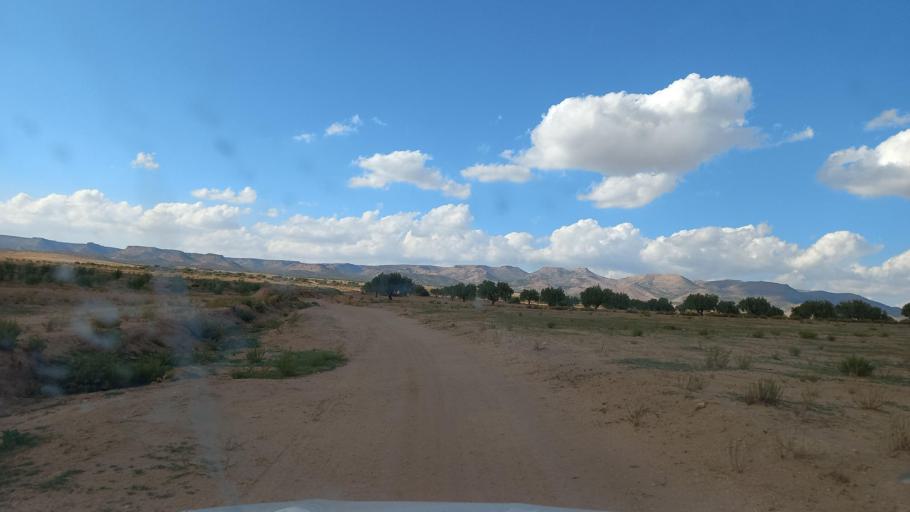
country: TN
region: Al Qasrayn
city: Sbiba
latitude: 35.3917
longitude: 9.0377
